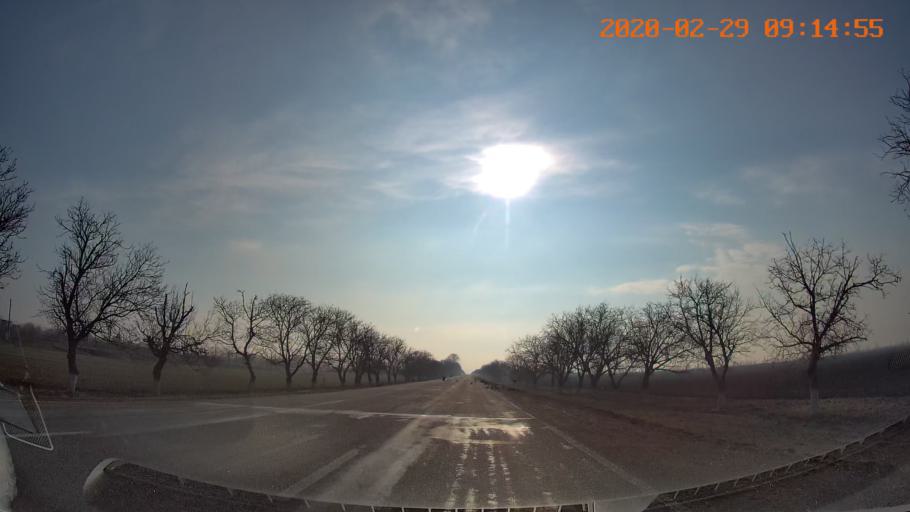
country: MD
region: Telenesti
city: Pervomaisc
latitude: 46.8047
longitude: 29.8608
